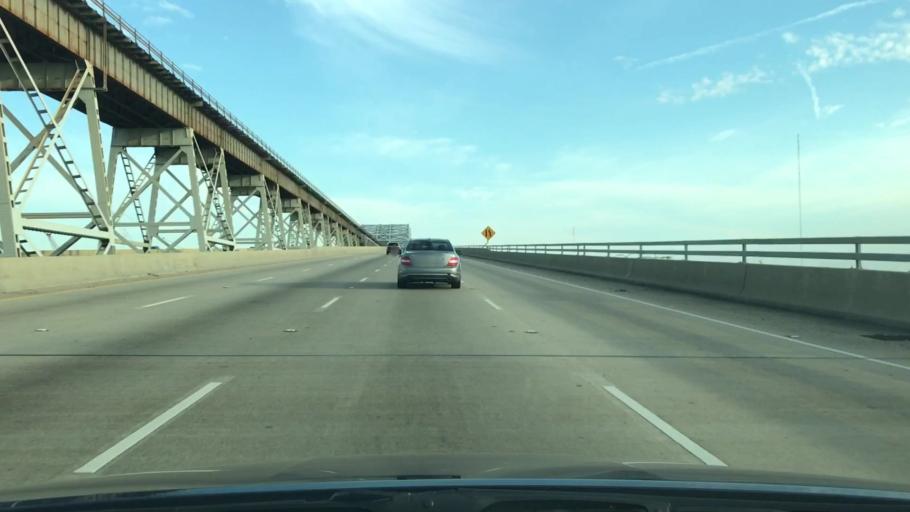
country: US
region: Louisiana
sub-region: Jefferson Parish
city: Elmwood
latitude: 29.9503
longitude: -90.1762
